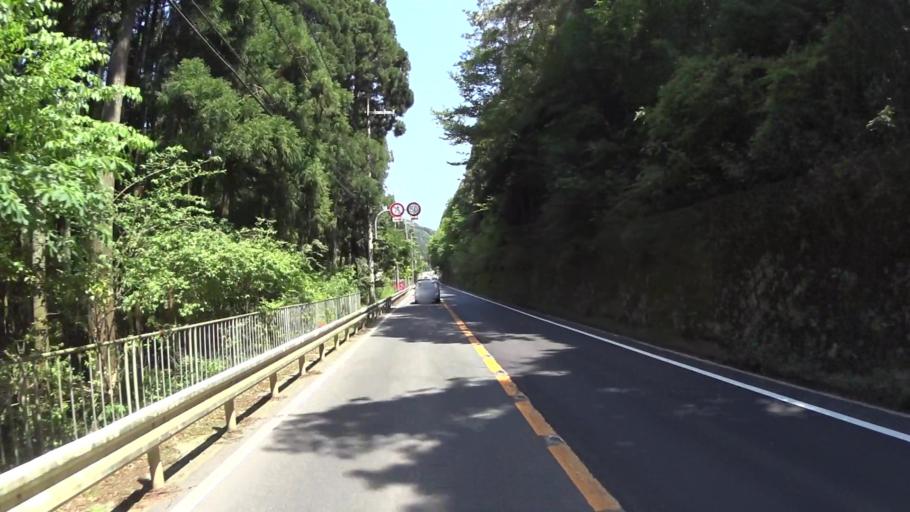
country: JP
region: Shiga Prefecture
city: Kitahama
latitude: 35.1244
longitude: 135.8340
